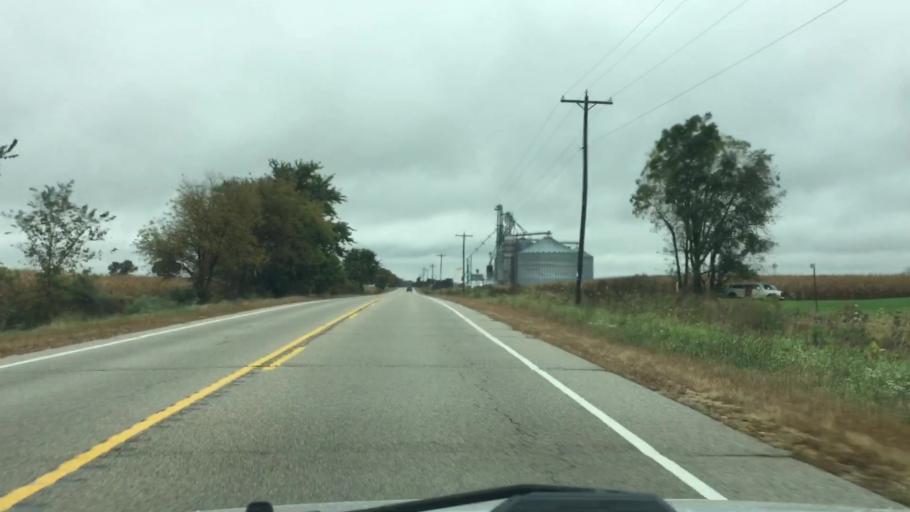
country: US
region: Wisconsin
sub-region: Walworth County
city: Whitewater
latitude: 42.8050
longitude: -88.7867
